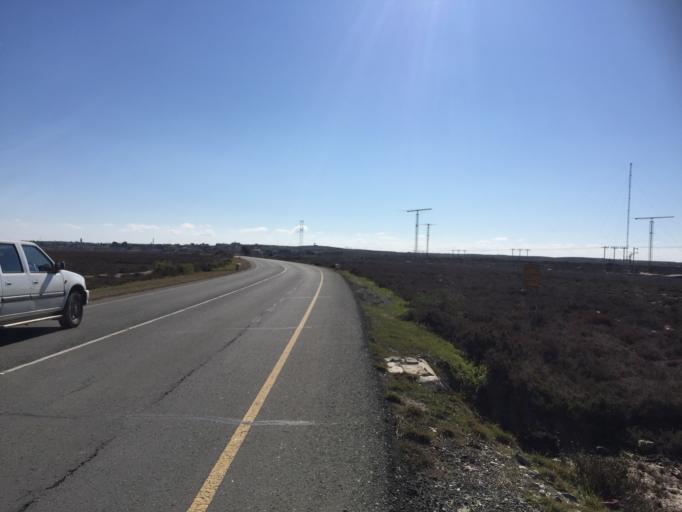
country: CY
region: Larnaka
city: Kolossi
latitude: 34.6143
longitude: 32.9438
